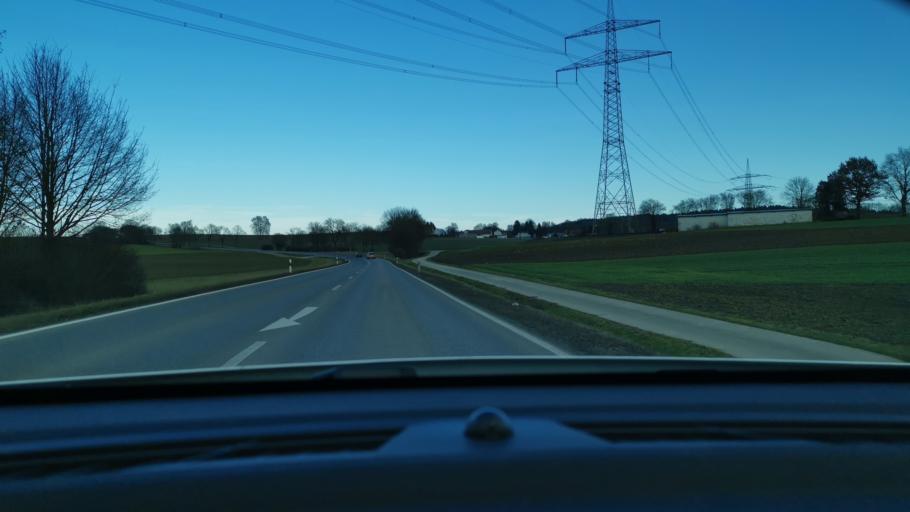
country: DE
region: Bavaria
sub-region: Swabia
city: Petersdorf
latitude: 48.5135
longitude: 11.0211
